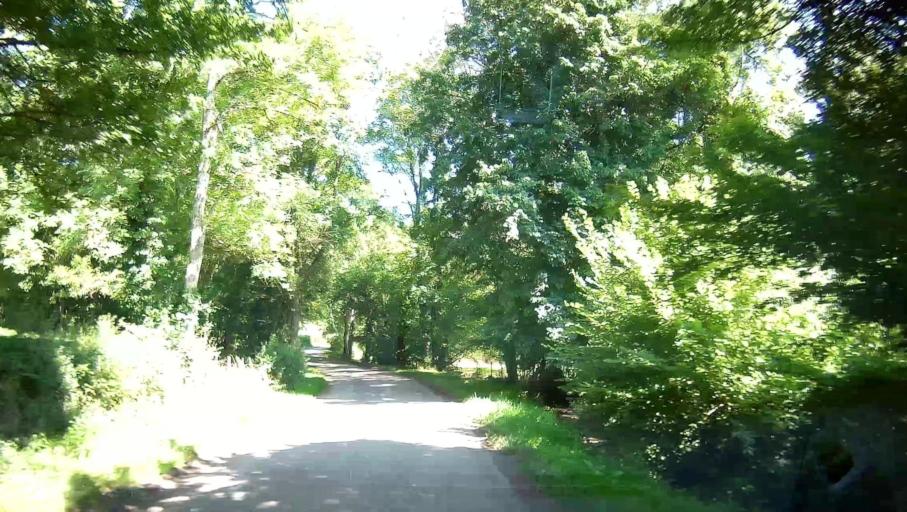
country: FR
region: Bourgogne
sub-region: Departement de la Cote-d'Or
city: Nolay
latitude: 46.9796
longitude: 4.6441
